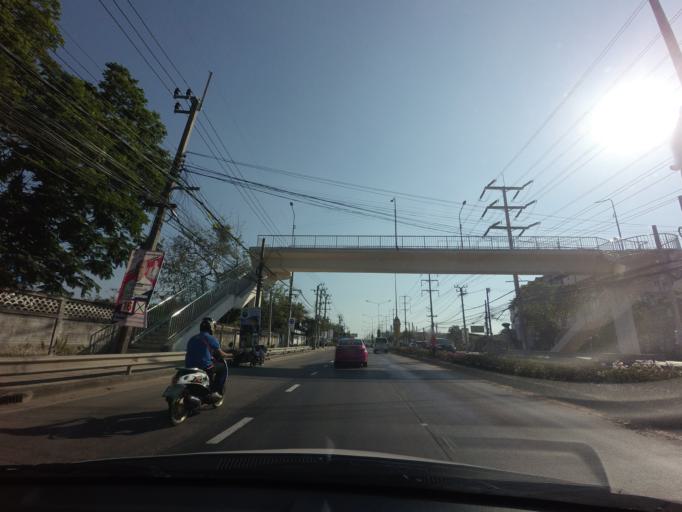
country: TH
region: Bangkok
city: Nong Chok
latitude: 13.8385
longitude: 100.8541
